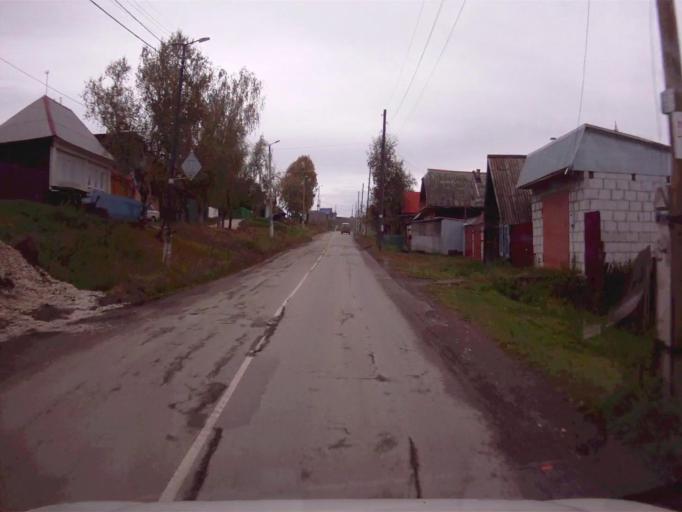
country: RU
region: Chelyabinsk
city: Nyazepetrovsk
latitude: 56.0587
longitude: 59.6099
